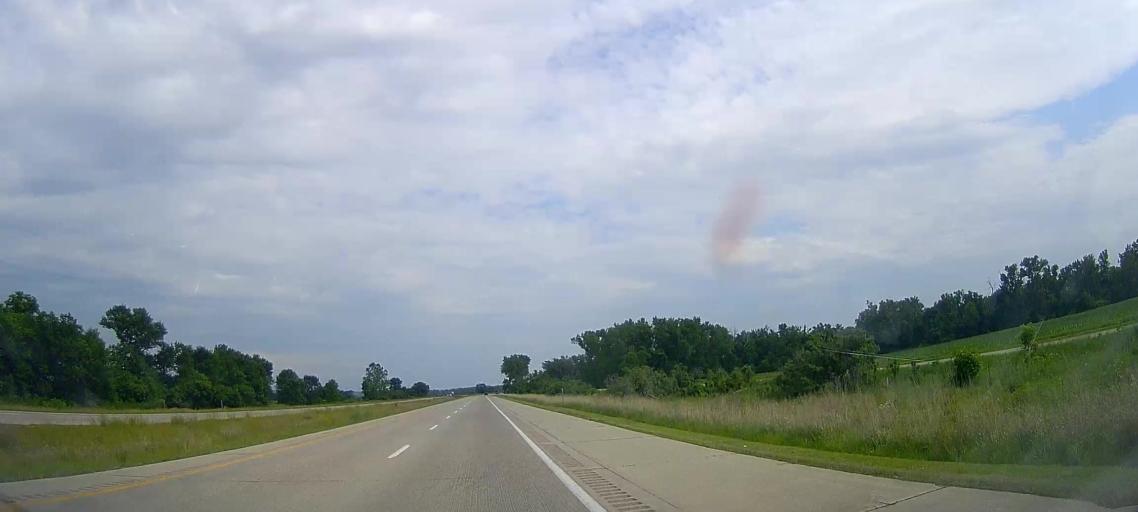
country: US
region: Nebraska
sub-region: Burt County
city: Tekamah
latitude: 41.8419
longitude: -96.0905
